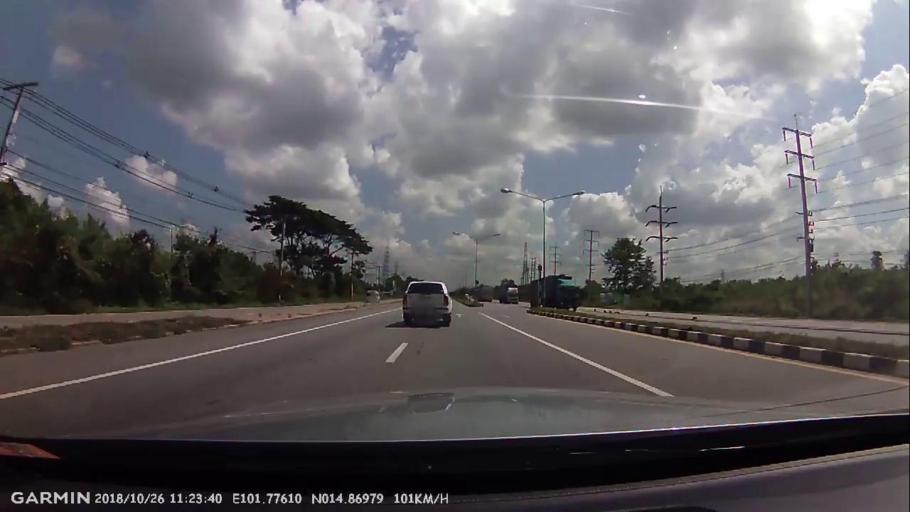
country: TH
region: Nakhon Ratchasima
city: Sung Noen
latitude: 14.8699
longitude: 101.7763
